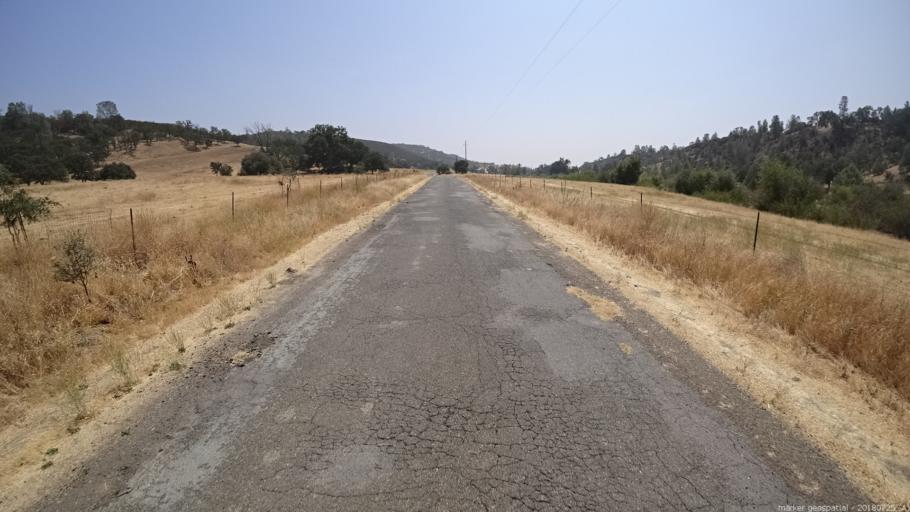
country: US
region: California
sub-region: Fresno County
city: Coalinga
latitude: 35.9452
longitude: -120.4679
